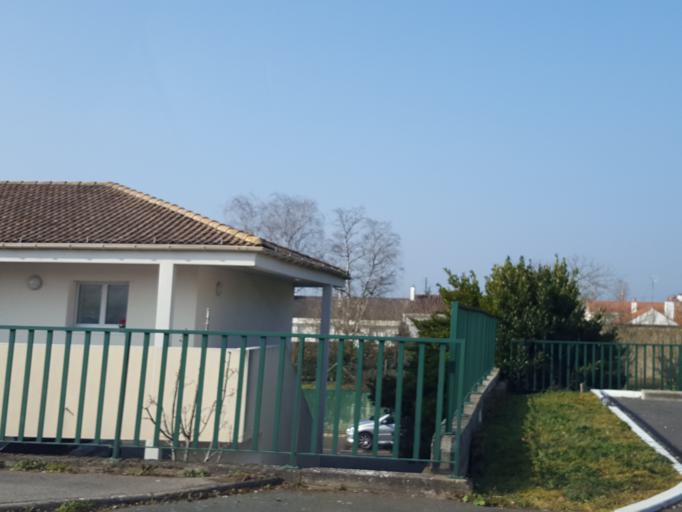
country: FR
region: Pays de la Loire
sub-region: Departement de la Vendee
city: La Roche-sur-Yon
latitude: 46.6651
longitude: -1.4529
